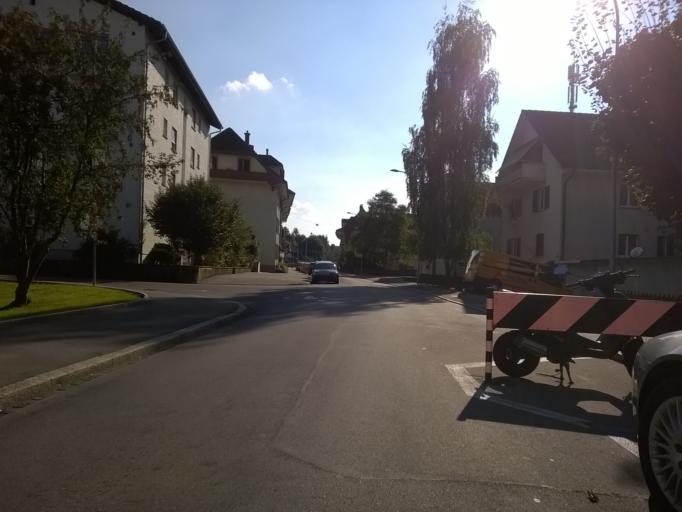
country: CH
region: Bern
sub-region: Bern-Mittelland District
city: Koniz
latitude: 46.9429
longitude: 7.3939
